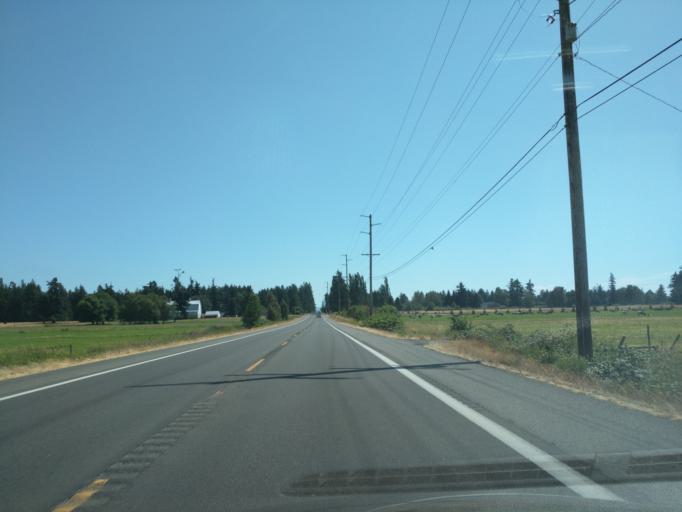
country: US
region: Washington
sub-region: Whatcom County
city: Lynden
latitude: 48.9022
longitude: -122.4423
